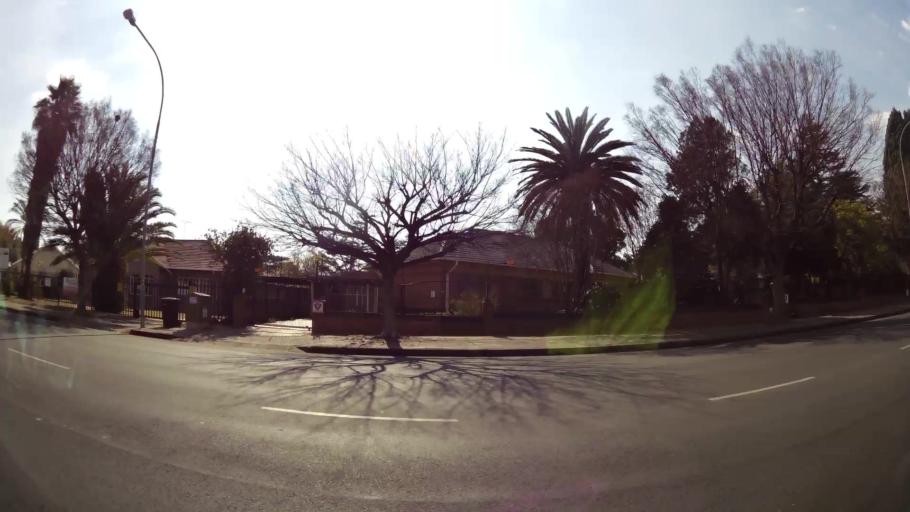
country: ZA
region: Gauteng
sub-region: City of Johannesburg Metropolitan Municipality
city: Modderfontein
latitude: -26.0920
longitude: 28.2285
